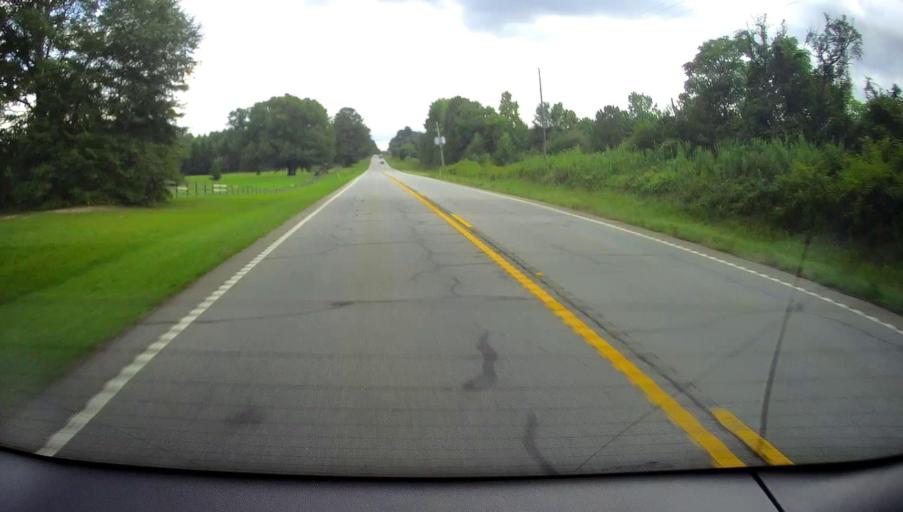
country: US
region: Georgia
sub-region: Coweta County
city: Senoia
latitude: 33.2012
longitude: -84.5803
